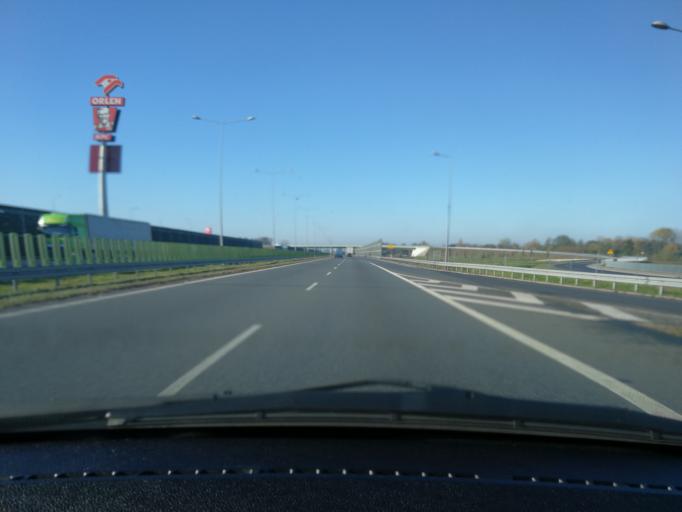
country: PL
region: Masovian Voivodeship
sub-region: Powiat zyrardowski
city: Zyrardow
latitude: 52.1100
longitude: 20.4613
